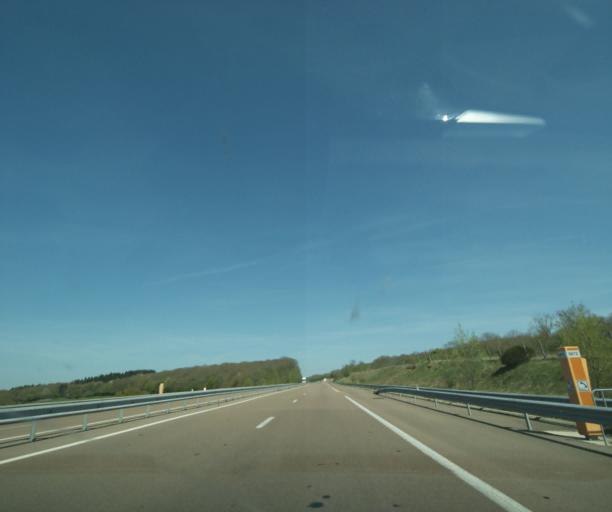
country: FR
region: Bourgogne
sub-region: Departement de la Nievre
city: Magny-Cours
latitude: 46.9139
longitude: 3.1606
